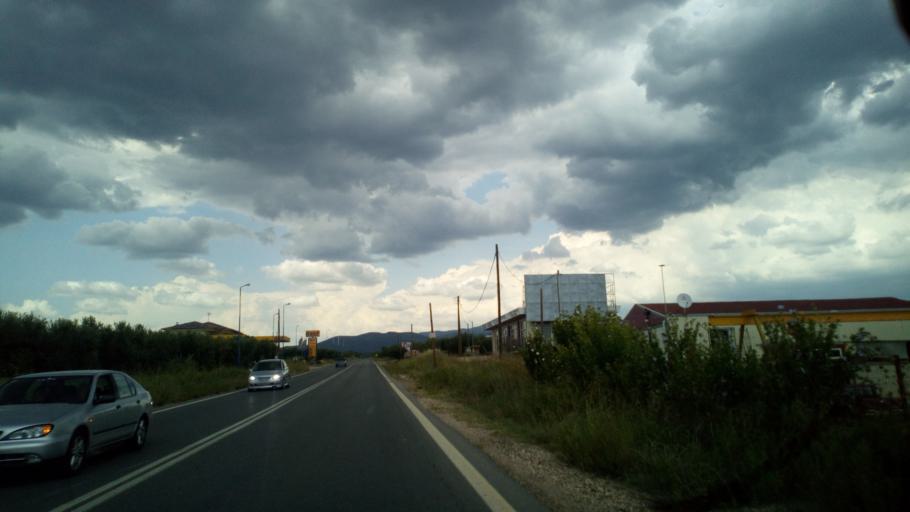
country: GR
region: Central Macedonia
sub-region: Nomos Chalkidikis
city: Kalyves Polygyrou
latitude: 40.2865
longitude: 23.4308
